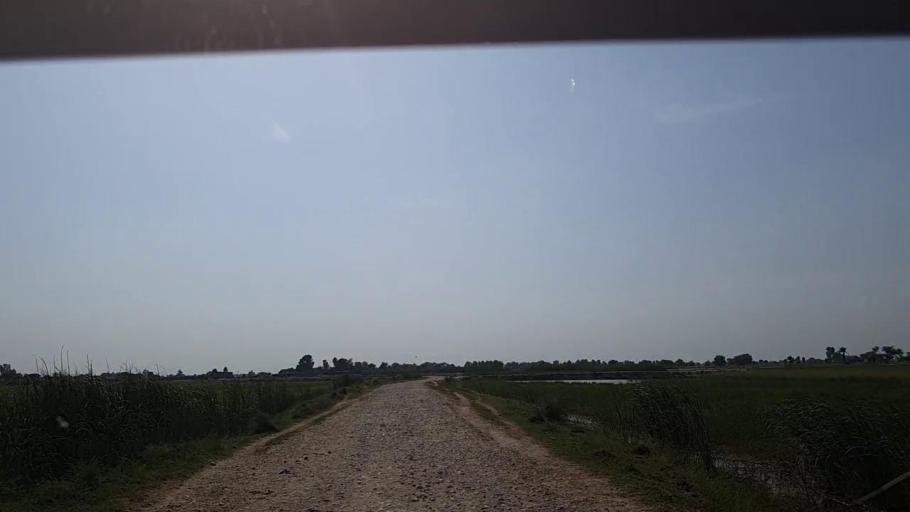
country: PK
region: Sindh
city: Khanpur
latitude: 27.8516
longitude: 69.3619
